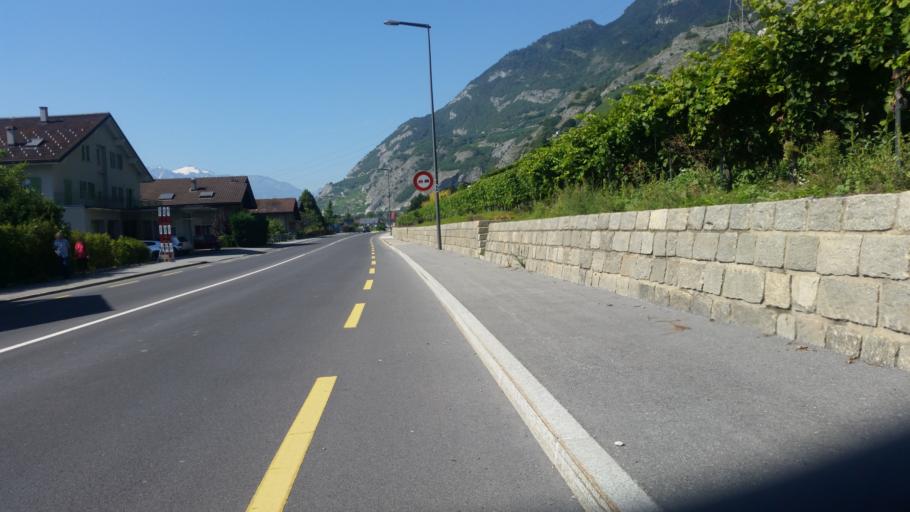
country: CH
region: Valais
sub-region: Conthey District
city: Vetroz
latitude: 46.2251
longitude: 7.2756
